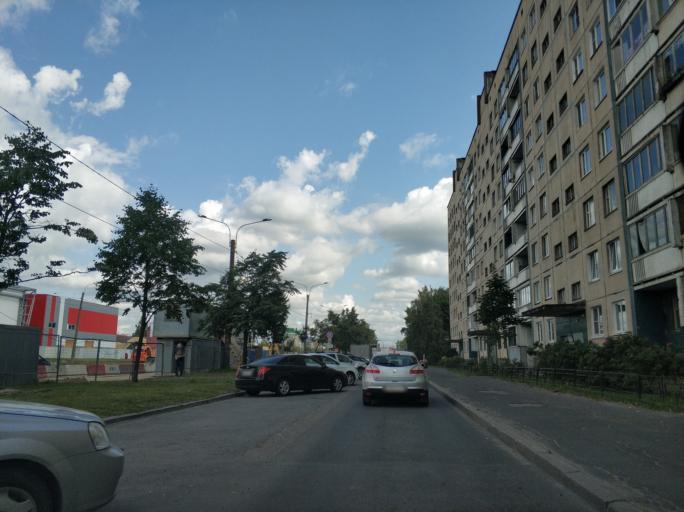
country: RU
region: St.-Petersburg
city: Krasnogvargeisky
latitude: 59.9603
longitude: 30.4842
